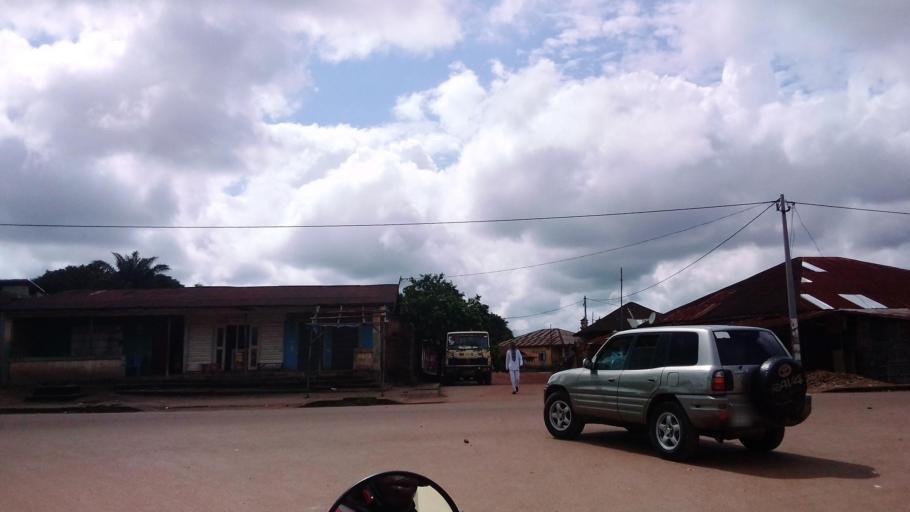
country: SL
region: Northern Province
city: Makeni
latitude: 8.8902
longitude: -12.0408
